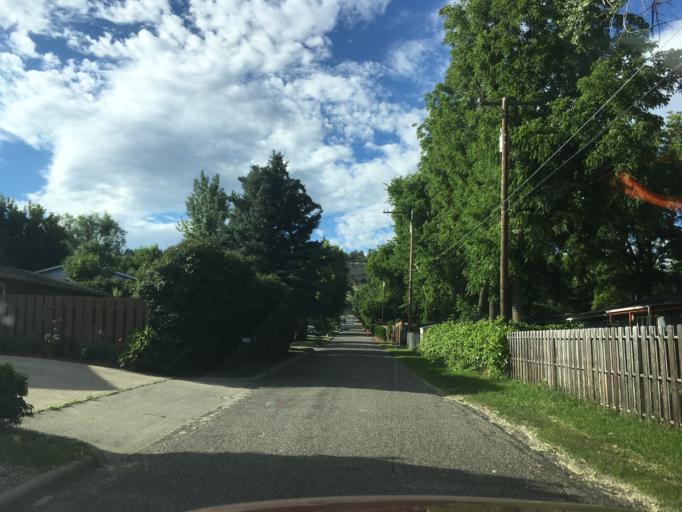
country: US
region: Montana
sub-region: Yellowstone County
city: Billings
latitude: 45.7957
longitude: -108.5749
